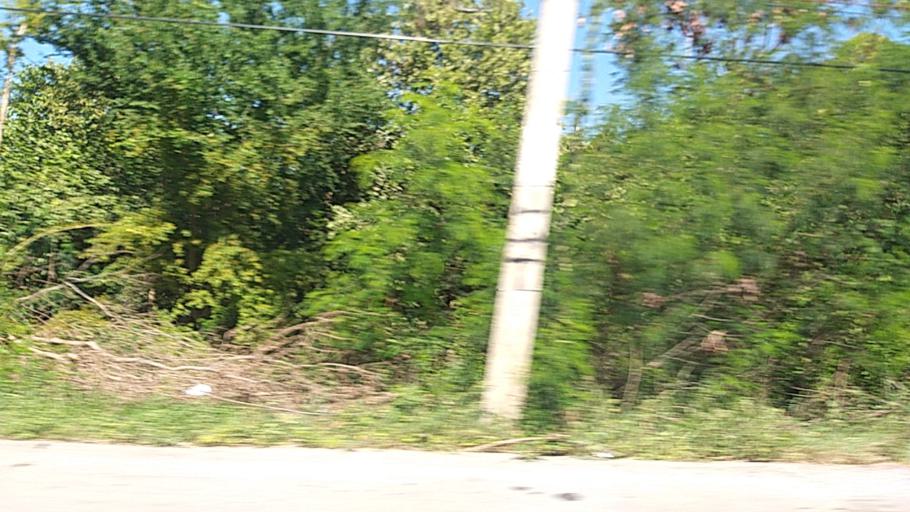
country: TH
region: Nakhon Ratchasima
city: Sung Noen
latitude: 14.8698
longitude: 101.7826
